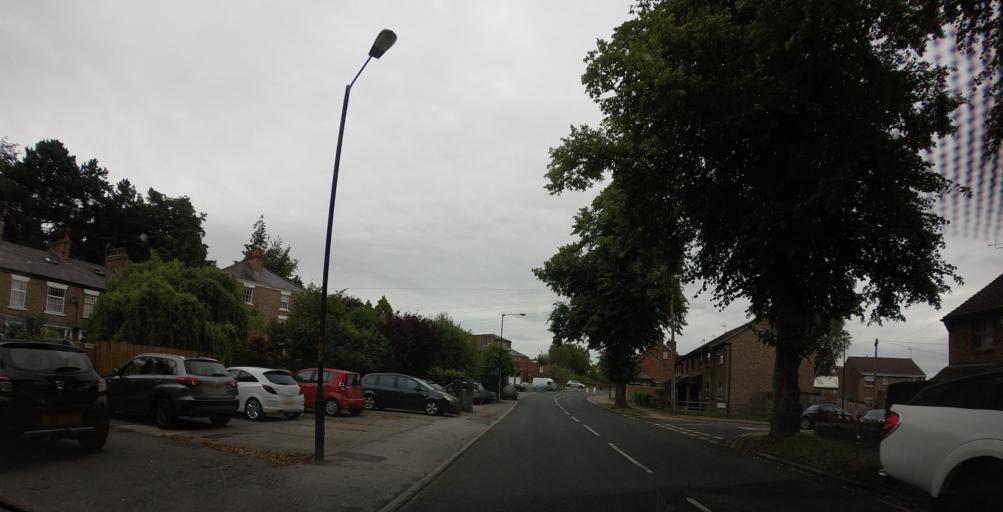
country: GB
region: England
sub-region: North Yorkshire
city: Ripon
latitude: 54.1347
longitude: -1.5279
